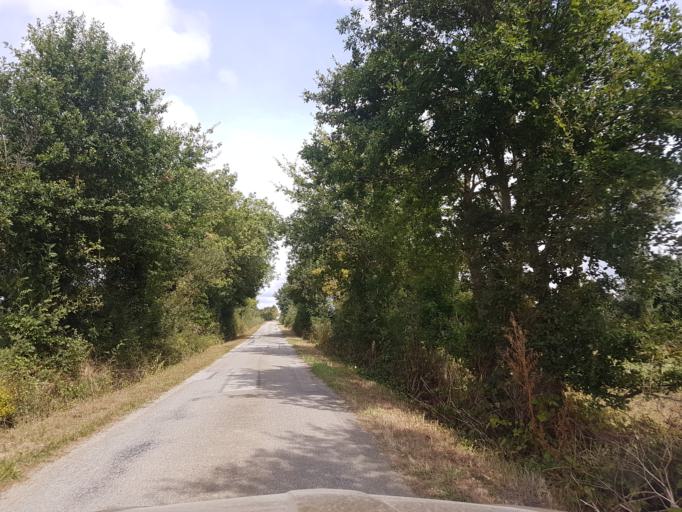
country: FR
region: Pays de la Loire
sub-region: Departement de la Loire-Atlantique
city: Petit-Mars
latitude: 47.4133
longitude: -1.4469
